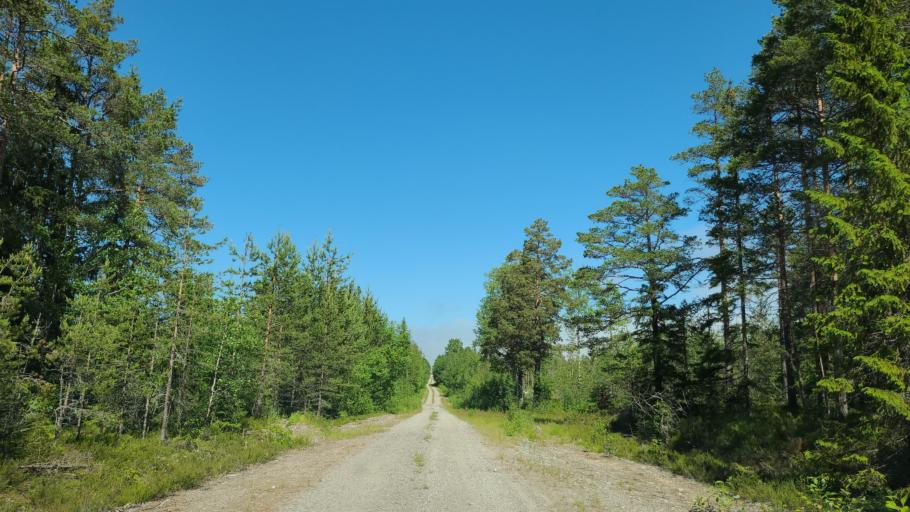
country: SE
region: Vaesternorrland
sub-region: OErnskoeldsviks Kommun
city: Husum
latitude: 63.4332
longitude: 19.2298
